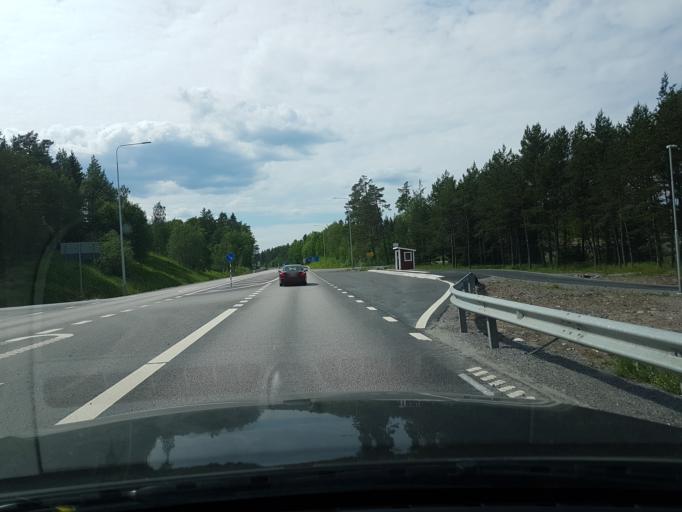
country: SE
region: Stockholm
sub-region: Norrtalje Kommun
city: Norrtalje
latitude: 59.7271
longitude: 18.8504
